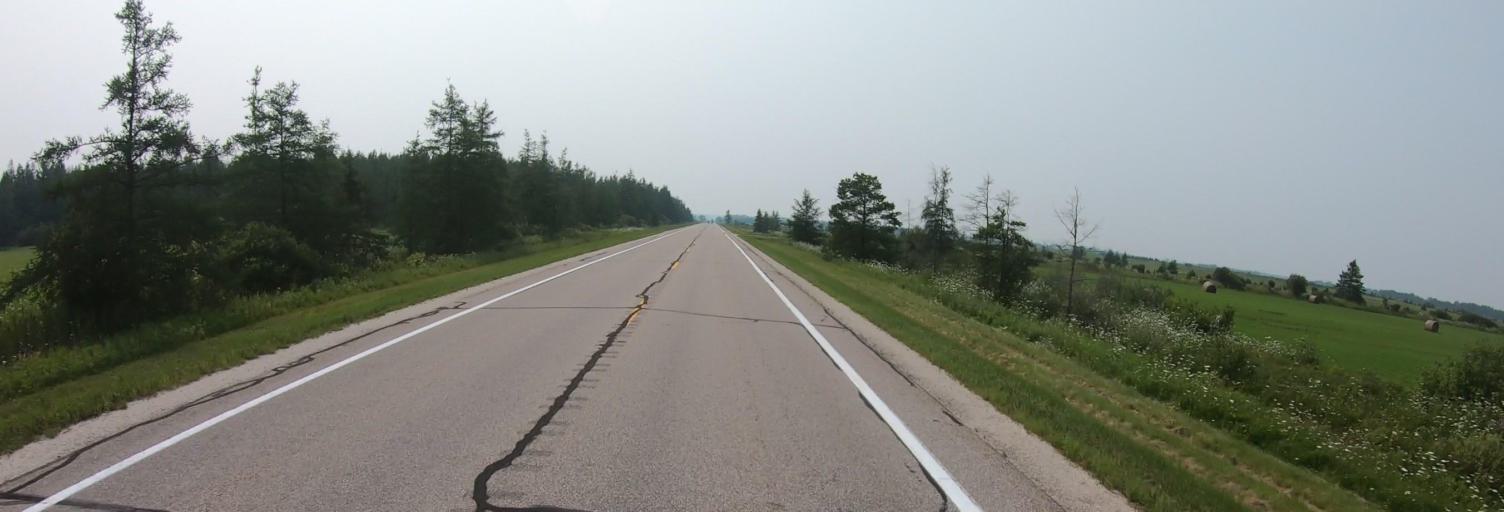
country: US
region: Michigan
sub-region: Chippewa County
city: Sault Ste. Marie
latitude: 46.1290
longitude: -84.3412
